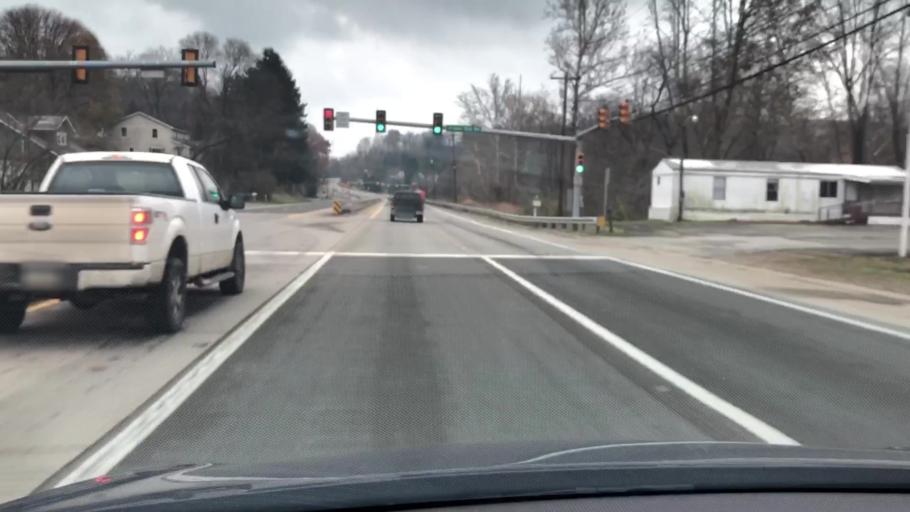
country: US
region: Pennsylvania
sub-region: Fayette County
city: Connellsville
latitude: 40.0446
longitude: -79.5736
